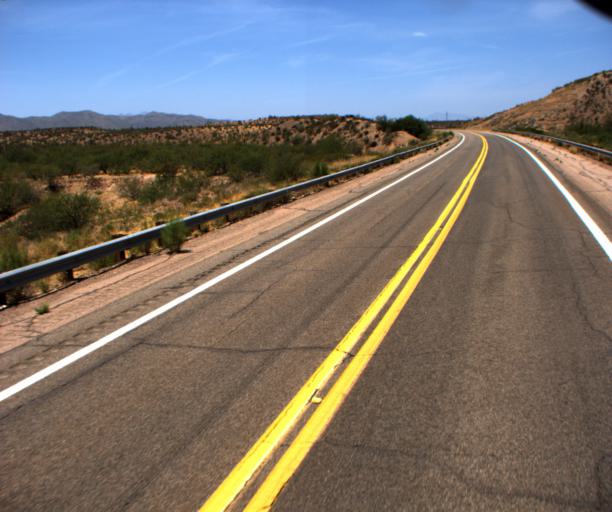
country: US
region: Arizona
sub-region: Gila County
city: Miami
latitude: 33.6086
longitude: -111.0119
